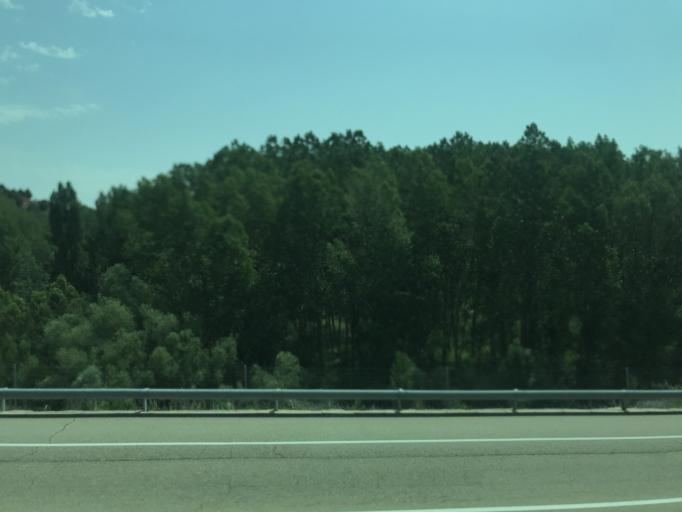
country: ES
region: Castille and Leon
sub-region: Provincia de Segovia
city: Castillejo de Mesleon
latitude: 41.2857
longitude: -3.6052
